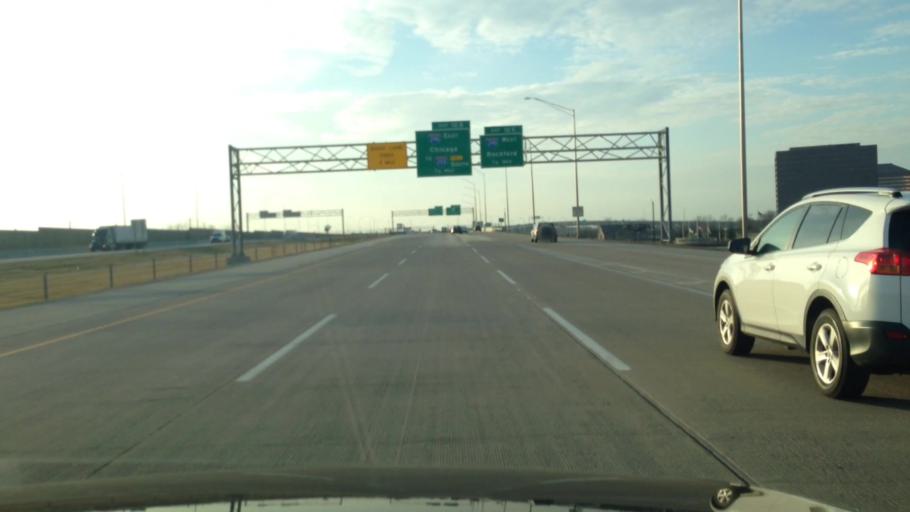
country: US
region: Illinois
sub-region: DuPage County
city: Itasca
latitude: 41.9843
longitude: -88.0093
